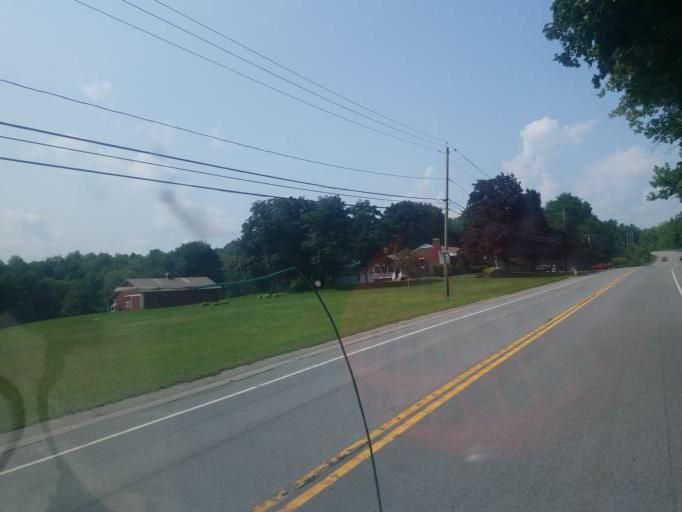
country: US
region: New York
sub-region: Montgomery County
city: Fonda
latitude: 42.9667
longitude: -74.3881
